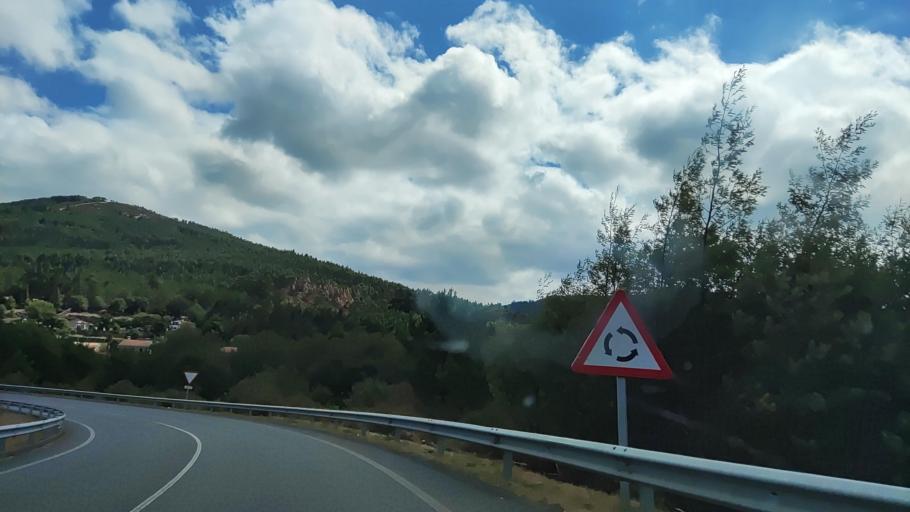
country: ES
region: Galicia
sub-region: Provincia da Coruna
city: Padron
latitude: 42.7825
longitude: -8.6545
